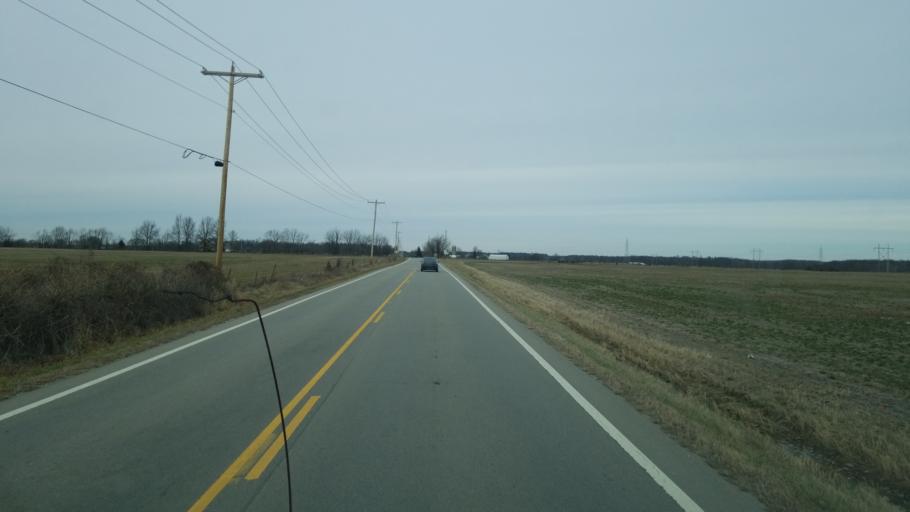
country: US
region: Ohio
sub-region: Adams County
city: Winchester
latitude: 39.0190
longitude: -83.7054
